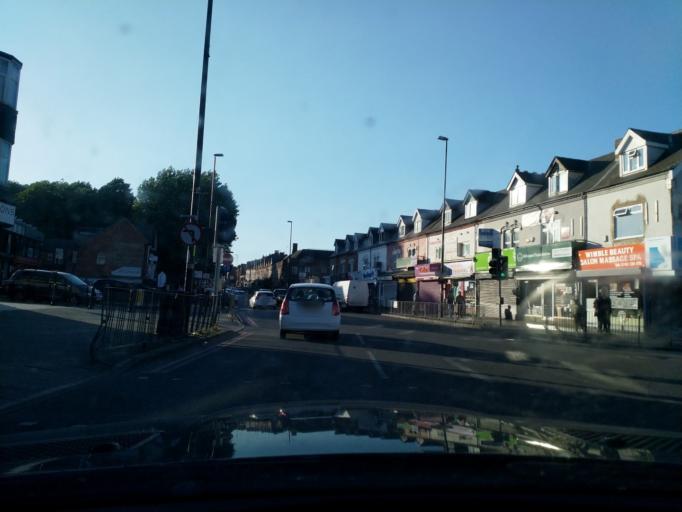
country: GB
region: England
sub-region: City and Borough of Birmingham
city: Acocks Green
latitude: 52.4473
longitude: -1.8605
